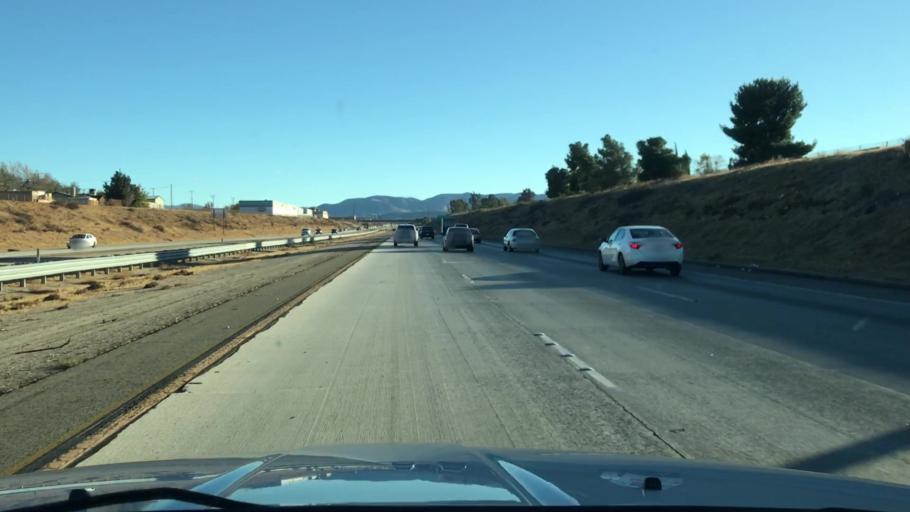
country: US
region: California
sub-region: Los Angeles County
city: Lancaster
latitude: 34.6552
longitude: -118.1535
